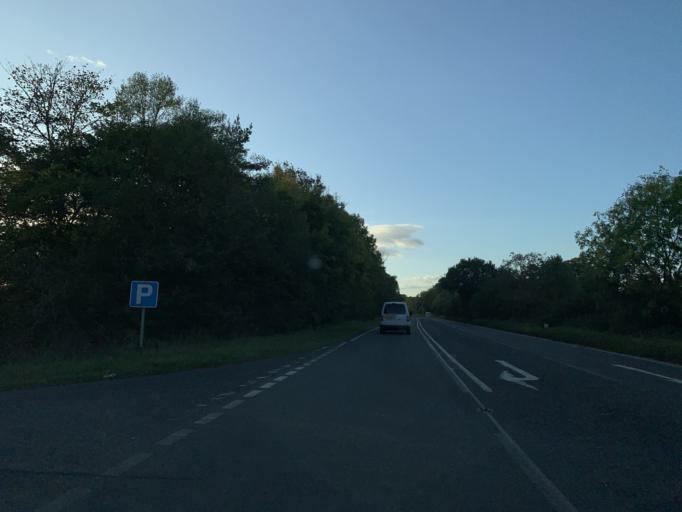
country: GB
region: England
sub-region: Wiltshire
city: Whiteparish
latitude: 50.9770
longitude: -1.6276
